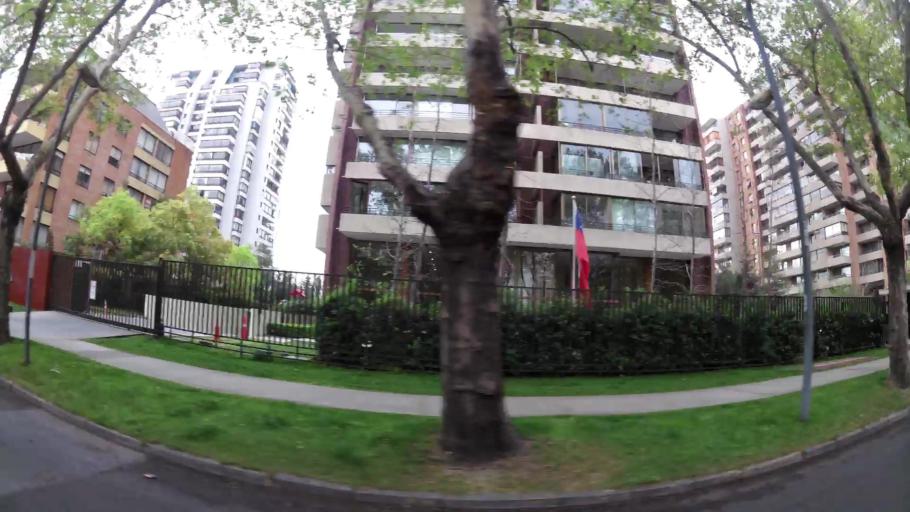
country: CL
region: Santiago Metropolitan
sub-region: Provincia de Santiago
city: Villa Presidente Frei, Nunoa, Santiago, Chile
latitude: -33.4242
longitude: -70.5825
